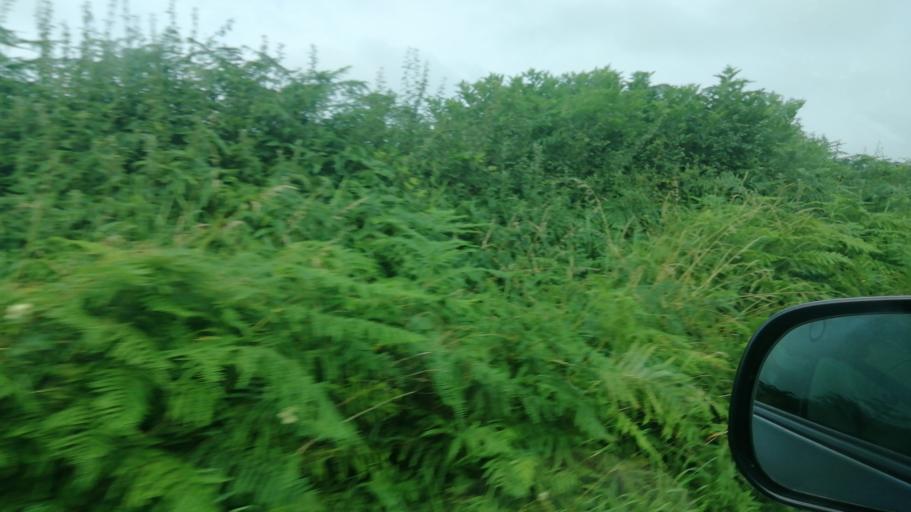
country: IE
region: Munster
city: Fethard
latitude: 52.5729
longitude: -7.5834
